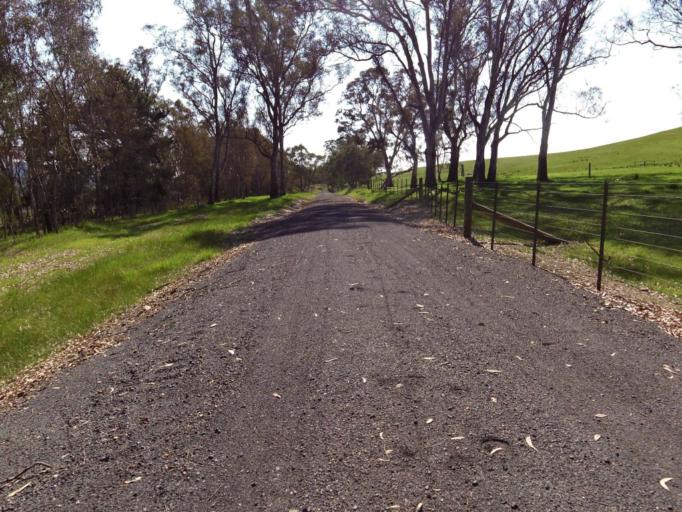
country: AU
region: Victoria
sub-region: Murrindindi
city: Alexandra
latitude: -37.1351
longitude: 145.5923
